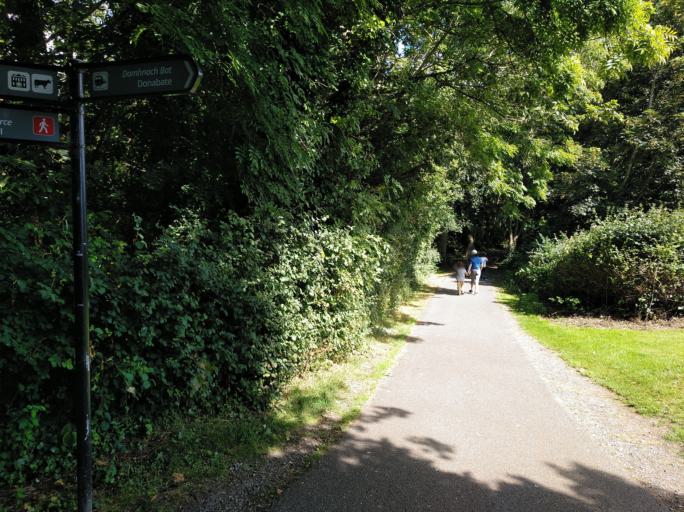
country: IE
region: Leinster
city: Donabate
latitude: 53.4848
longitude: -6.1574
